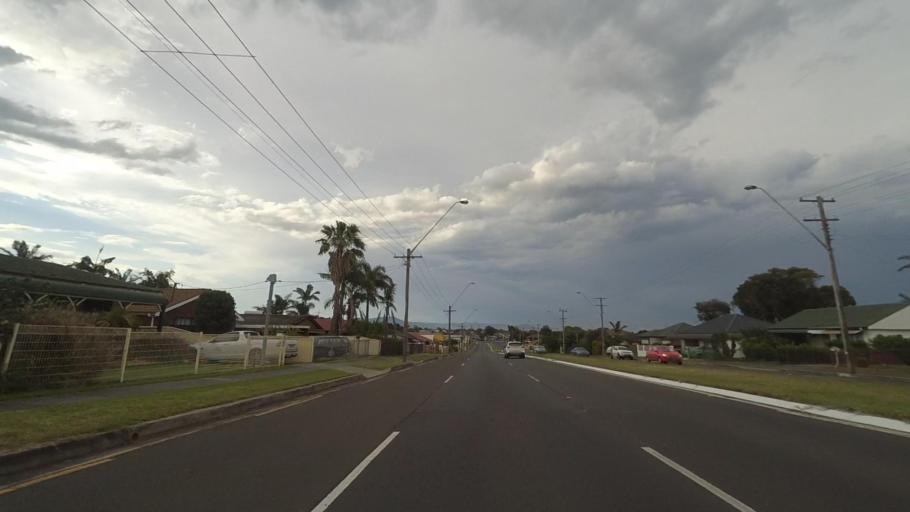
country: AU
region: New South Wales
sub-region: Shellharbour
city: Barrack Heights
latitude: -34.5614
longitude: 150.8600
